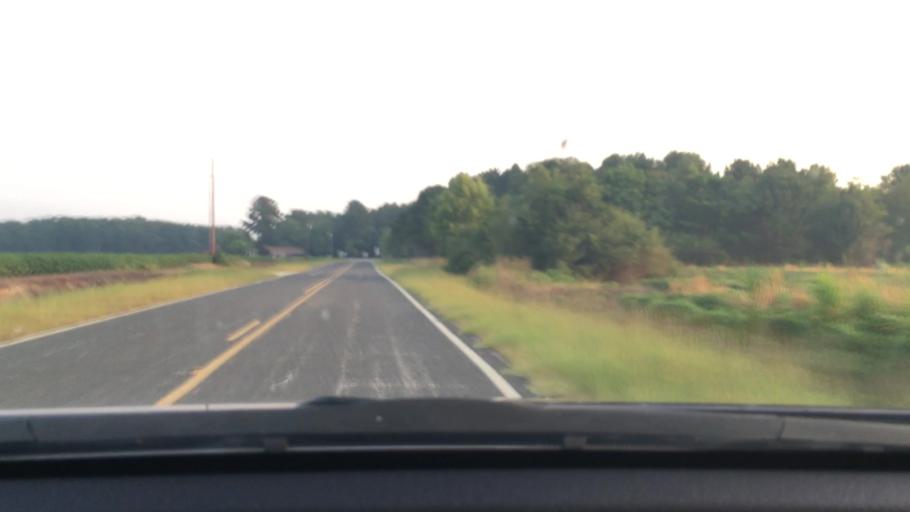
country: US
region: South Carolina
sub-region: Lee County
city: Bishopville
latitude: 34.2655
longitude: -80.1370
